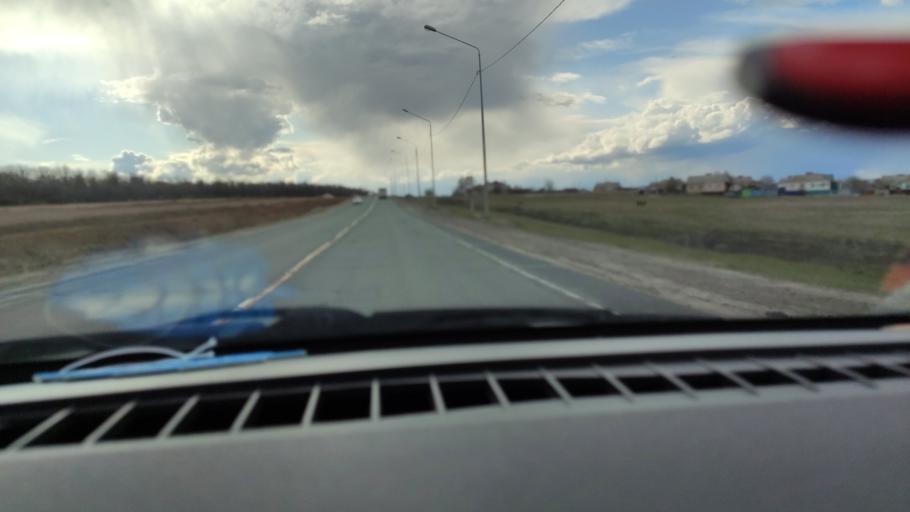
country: RU
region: Saratov
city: Sennoy
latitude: 52.1587
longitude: 47.0633
